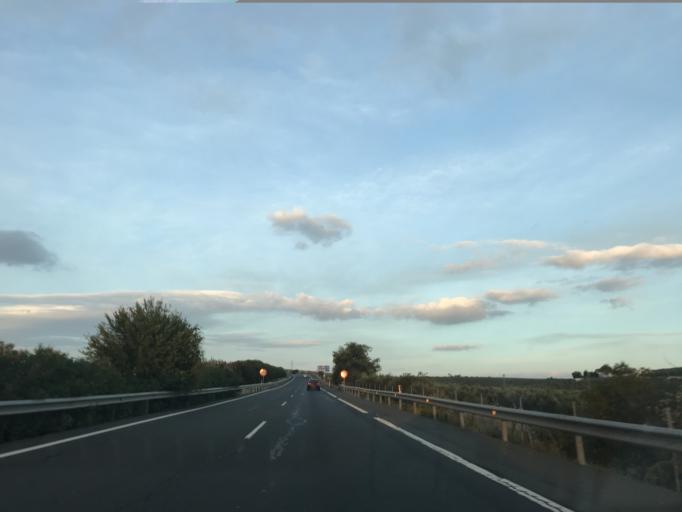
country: ES
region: Andalusia
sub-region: Province of Cordoba
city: La Victoria
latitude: 37.7537
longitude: -4.8362
